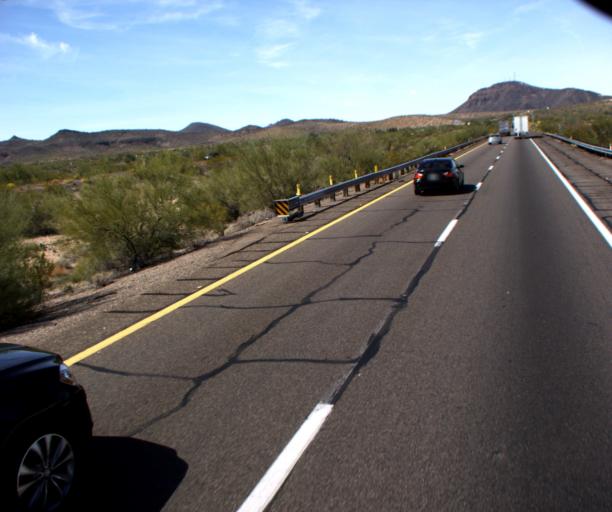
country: US
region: Arizona
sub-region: La Paz County
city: Quartzsite
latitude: 33.6622
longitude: -114.0123
